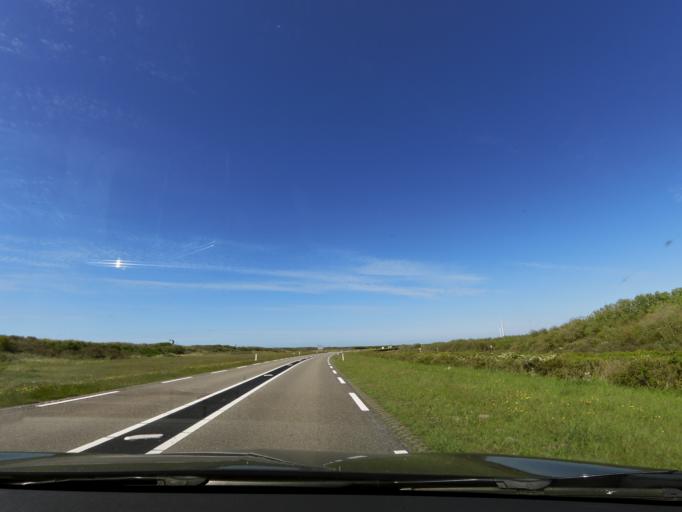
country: NL
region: Zeeland
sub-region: Schouwen-Duiveland
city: Scharendijke
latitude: 51.7496
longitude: 3.8270
